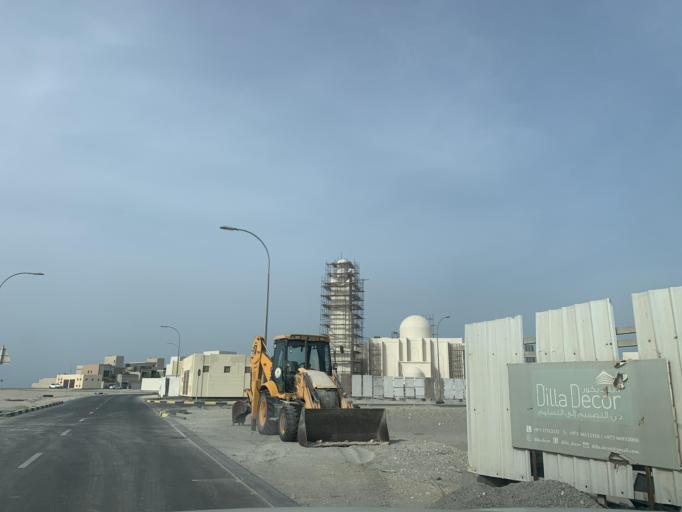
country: BH
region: Muharraq
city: Al Muharraq
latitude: 26.3220
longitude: 50.6247
